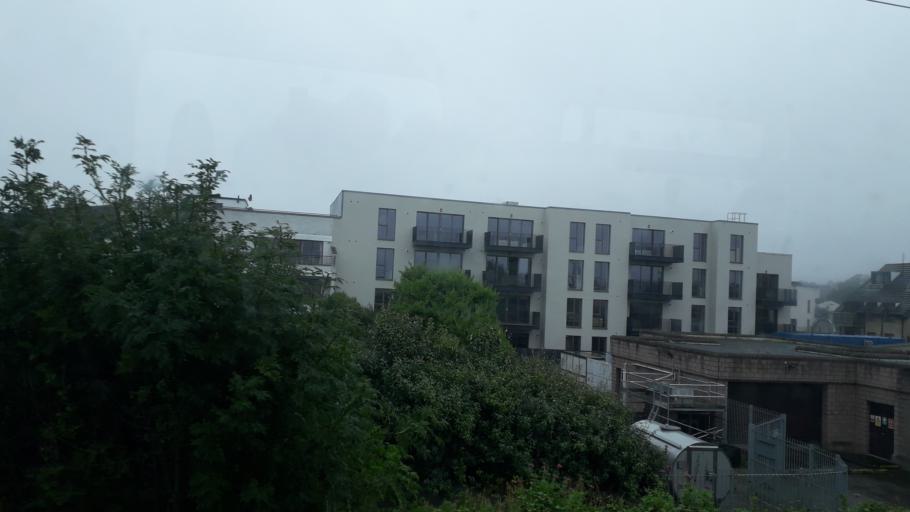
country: IE
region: Leinster
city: Malahide
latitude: 53.4529
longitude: -6.1562
